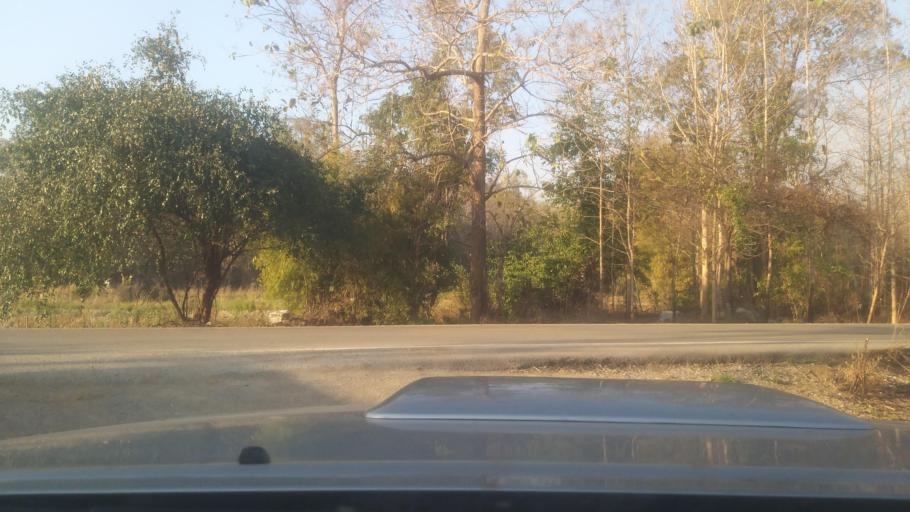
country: TH
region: Phrae
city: Nong Muang Khai
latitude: 18.2947
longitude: 100.0374
